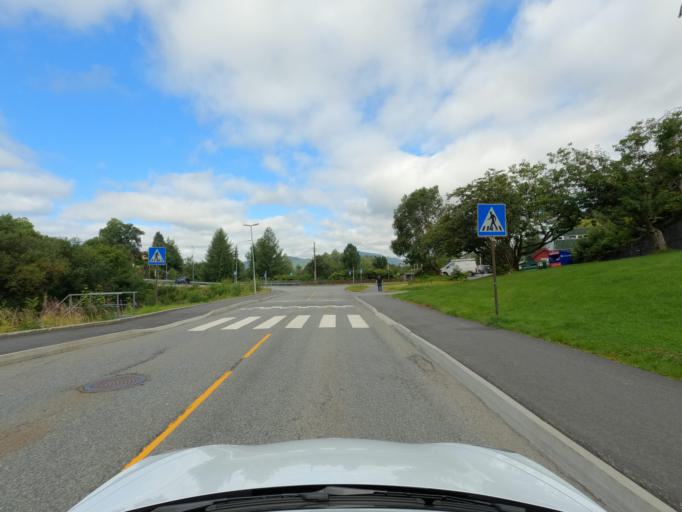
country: NO
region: Hordaland
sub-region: Bergen
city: Sandsli
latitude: 60.3099
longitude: 5.3630
